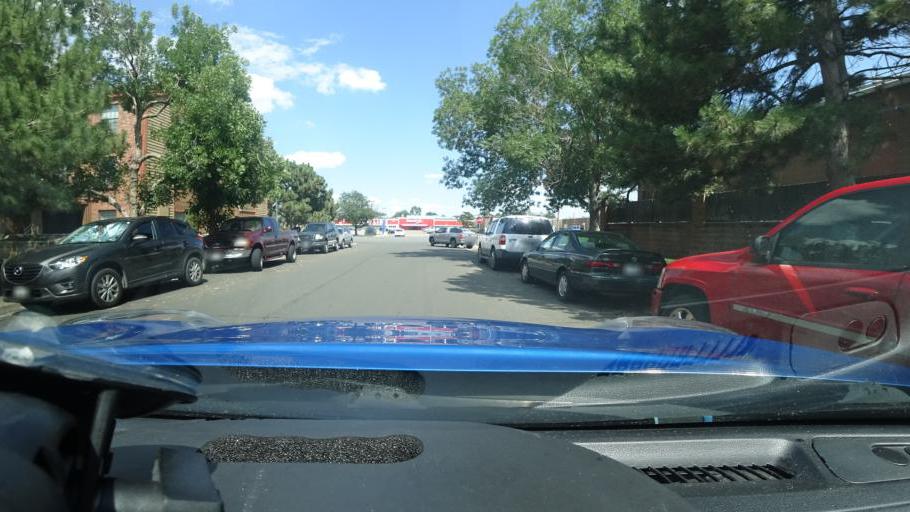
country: US
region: Colorado
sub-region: Adams County
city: Aurora
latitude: 39.6767
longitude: -104.8480
